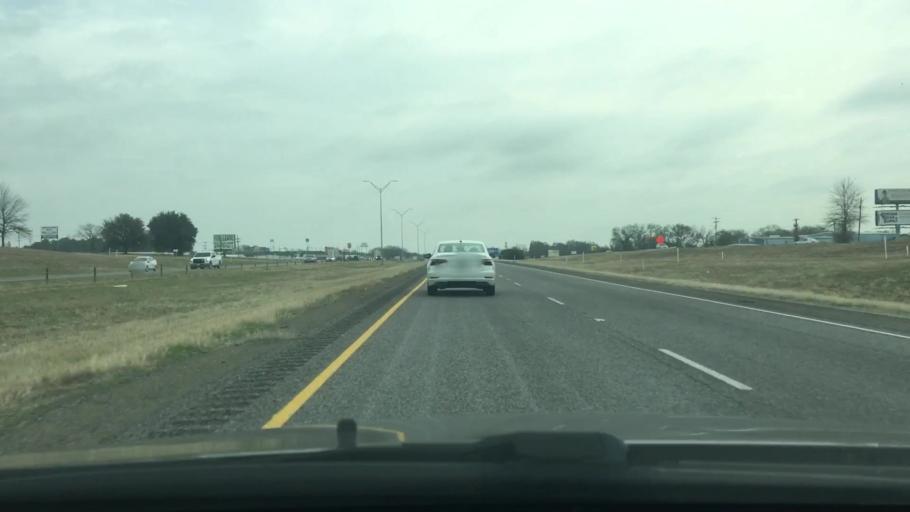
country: US
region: Texas
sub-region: Freestone County
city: Fairfield
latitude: 31.7264
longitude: -96.1805
